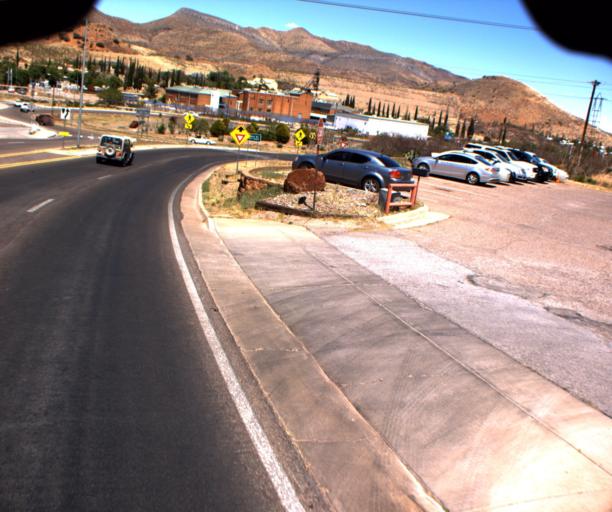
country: US
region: Arizona
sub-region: Cochise County
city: Bisbee
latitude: 31.4274
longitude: -109.8933
